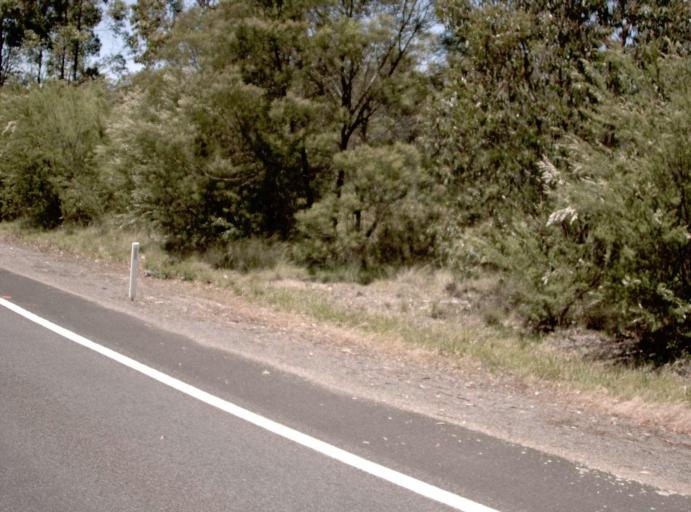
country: AU
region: Victoria
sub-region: East Gippsland
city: Lakes Entrance
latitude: -37.7512
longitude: 148.3612
